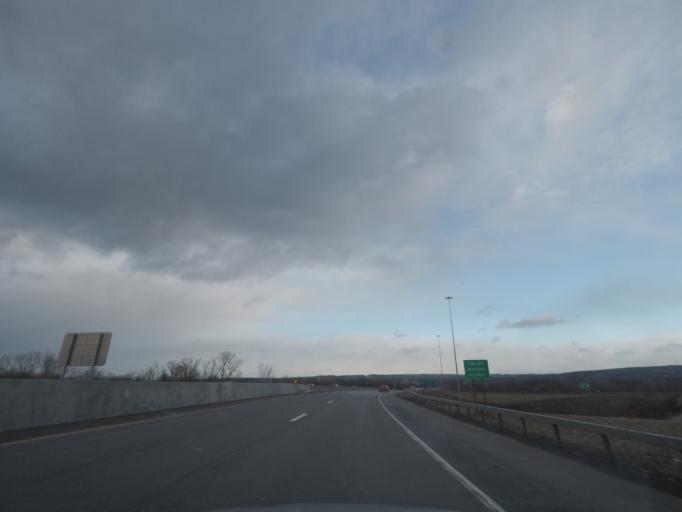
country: US
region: New York
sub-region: Oneida County
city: Utica
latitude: 43.1073
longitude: -75.2387
